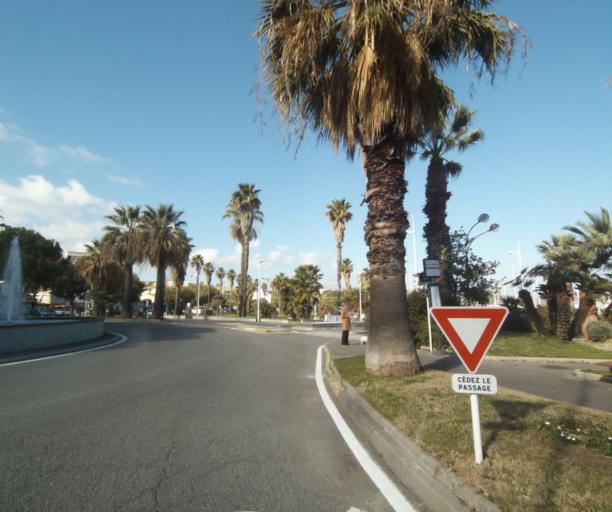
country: FR
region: Provence-Alpes-Cote d'Azur
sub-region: Departement des Alpes-Maritimes
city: Antibes
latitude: 43.5844
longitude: 7.1223
